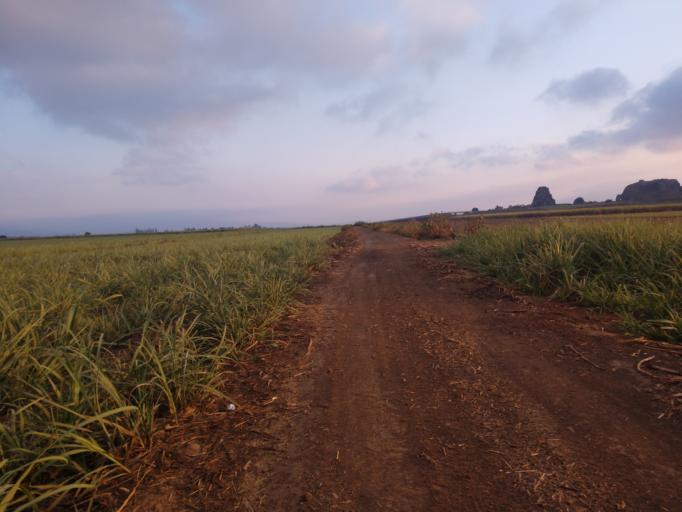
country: MX
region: Nayarit
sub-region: Tepic
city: La Corregidora
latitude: 21.4819
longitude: -104.8053
